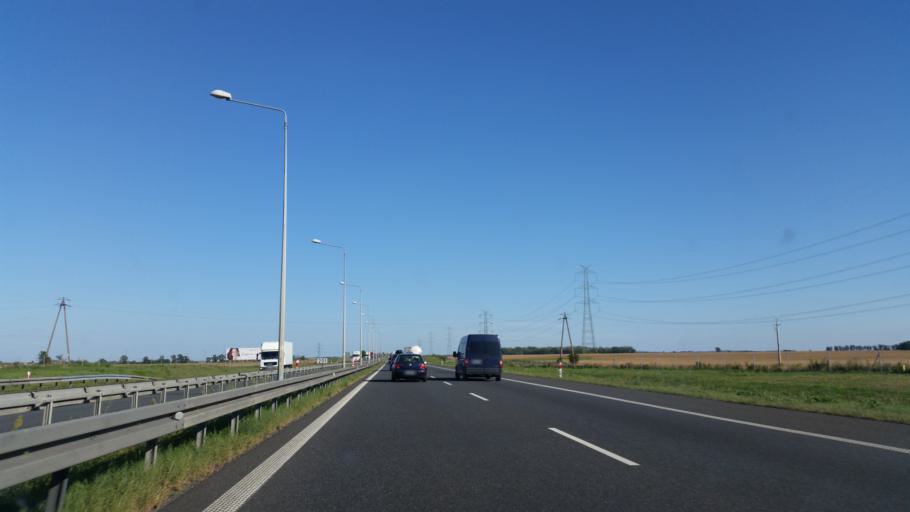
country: PL
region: Opole Voivodeship
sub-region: Powiat brzeski
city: Olszanka
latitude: 50.7546
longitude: 17.4344
